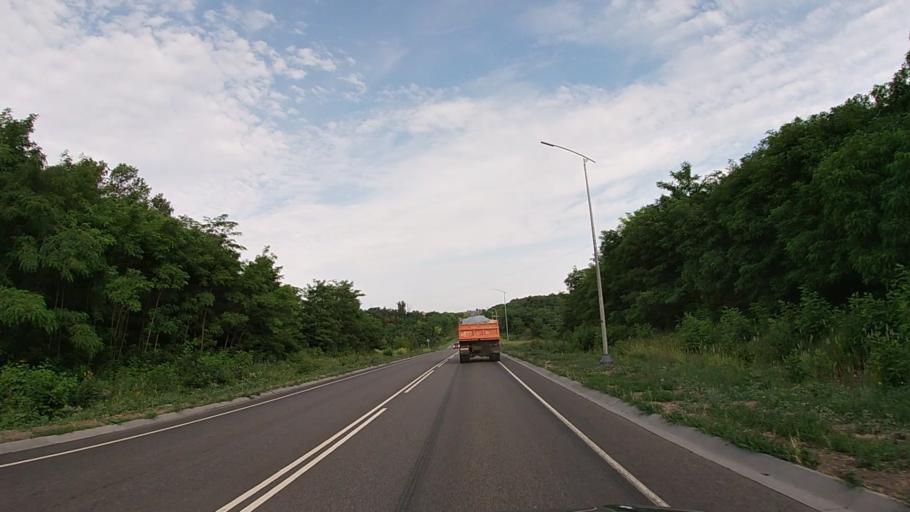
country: RU
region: Belgorod
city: Severnyy
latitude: 50.6675
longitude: 36.4927
